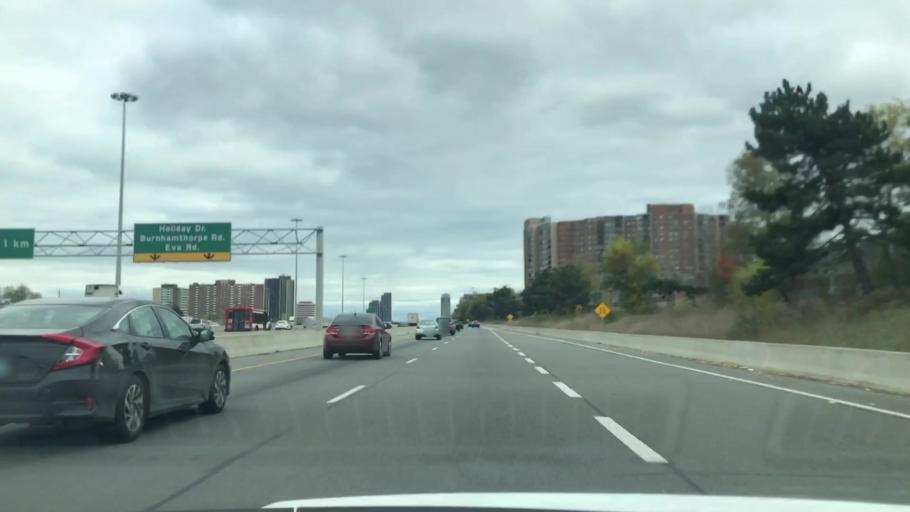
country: CA
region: Ontario
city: Etobicoke
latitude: 43.6608
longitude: -79.5712
